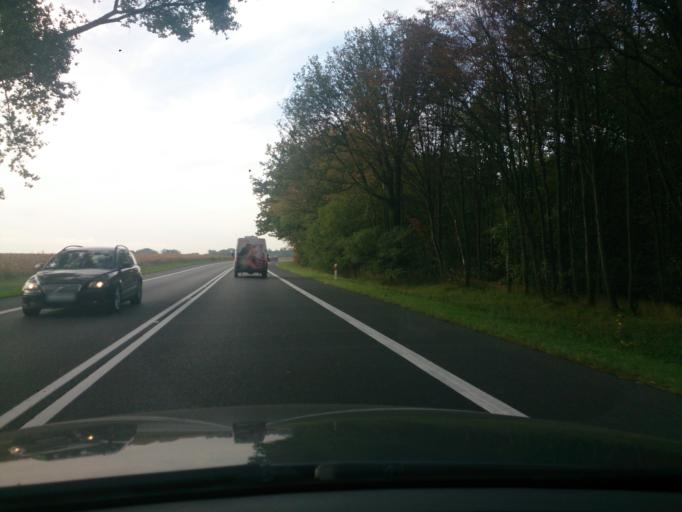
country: PL
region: Kujawsko-Pomorskie
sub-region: Powiat swiecki
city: Pruszcz
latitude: 53.3293
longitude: 18.2882
